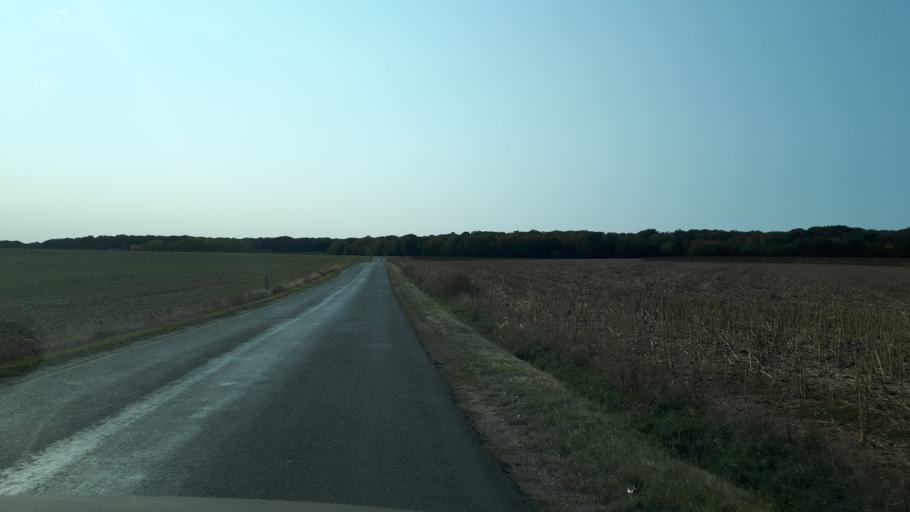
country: FR
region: Centre
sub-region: Departement du Cher
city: Rians
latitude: 47.1855
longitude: 2.6557
